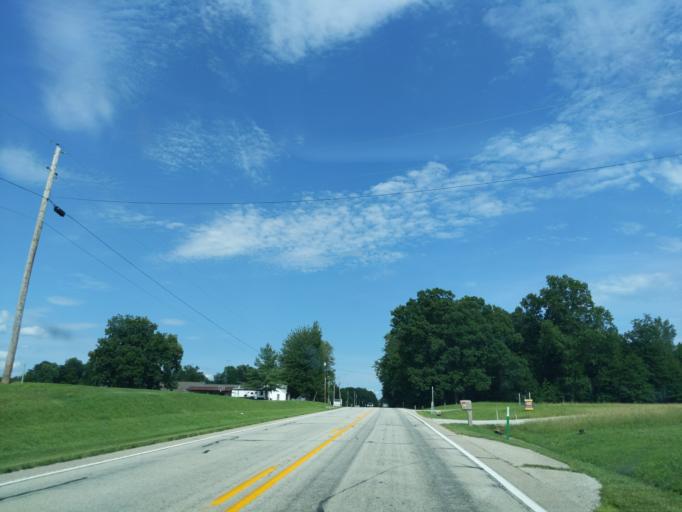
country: US
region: Indiana
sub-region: Ripley County
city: Sunman
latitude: 39.2784
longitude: -85.1339
